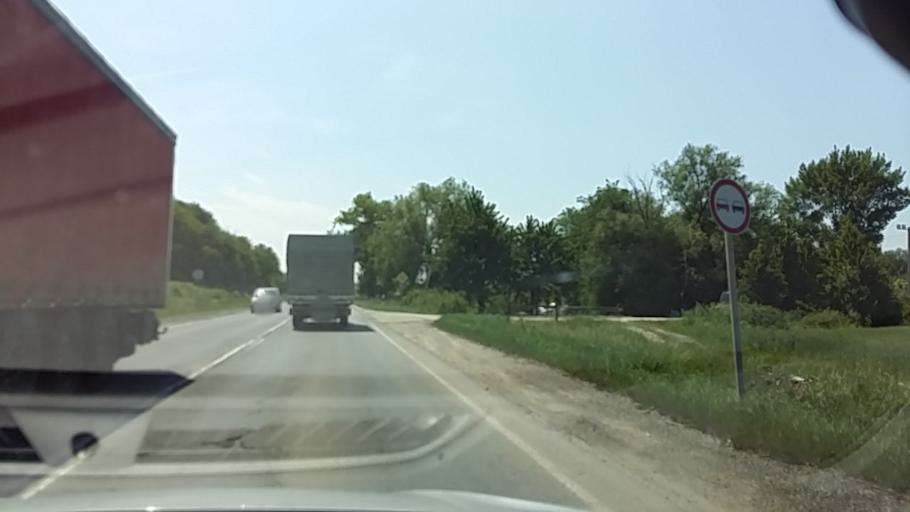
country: HU
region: Gyor-Moson-Sopron
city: Sopron
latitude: 47.6531
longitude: 16.6307
